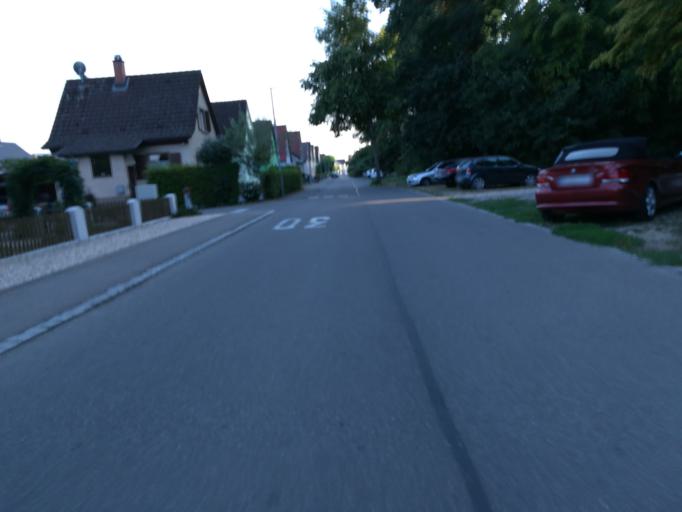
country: DE
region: Baden-Wuerttemberg
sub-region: Freiburg Region
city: Rielasingen-Worblingen
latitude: 47.7401
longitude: 8.8453
